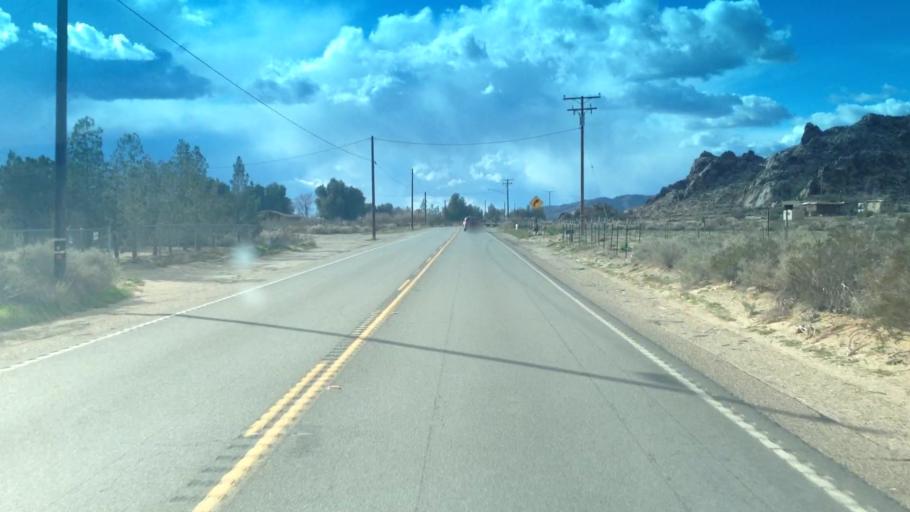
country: US
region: California
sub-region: San Bernardino County
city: Lucerne Valley
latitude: 34.4440
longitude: -116.9837
